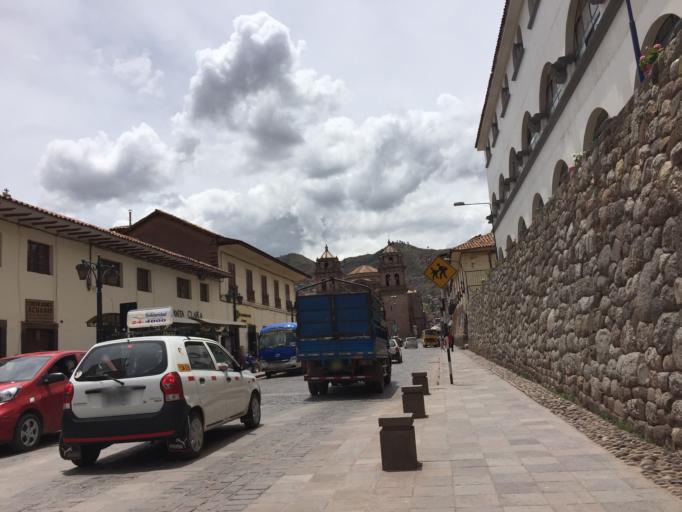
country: PE
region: Cusco
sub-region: Provincia de Cusco
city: Cusco
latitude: -13.5198
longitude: -71.9823
